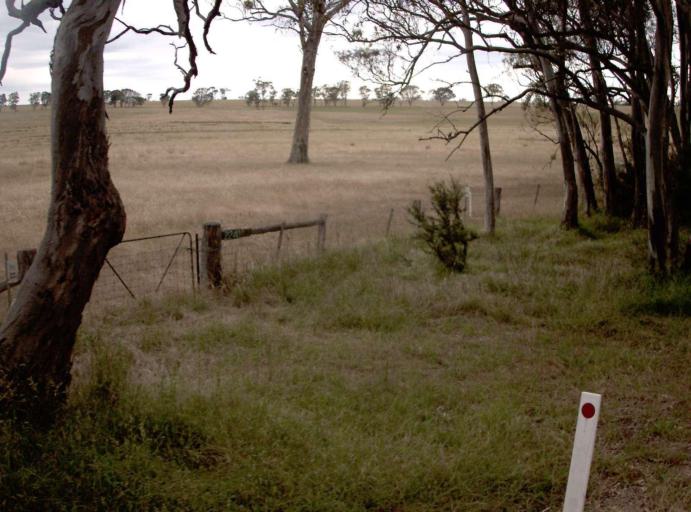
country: AU
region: Victoria
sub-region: East Gippsland
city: Bairnsdale
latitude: -37.9820
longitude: 147.4098
